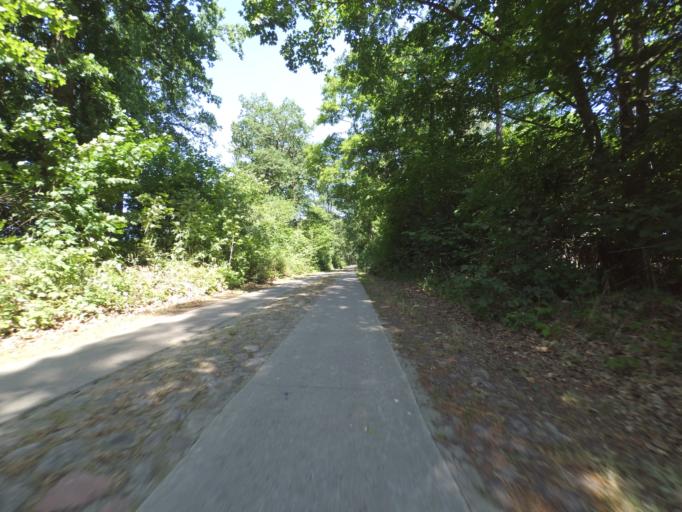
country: DE
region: Brandenburg
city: Heiligengrabe
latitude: 53.2363
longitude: 12.3157
